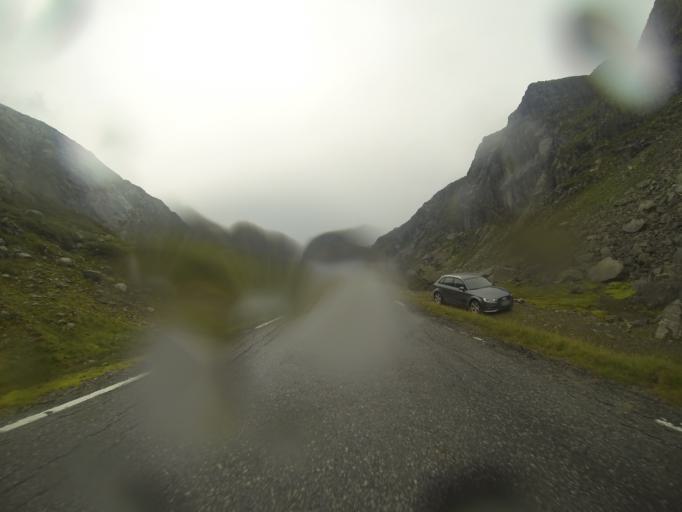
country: NO
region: Hordaland
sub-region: Odda
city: Odda
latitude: 59.7709
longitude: 6.7421
